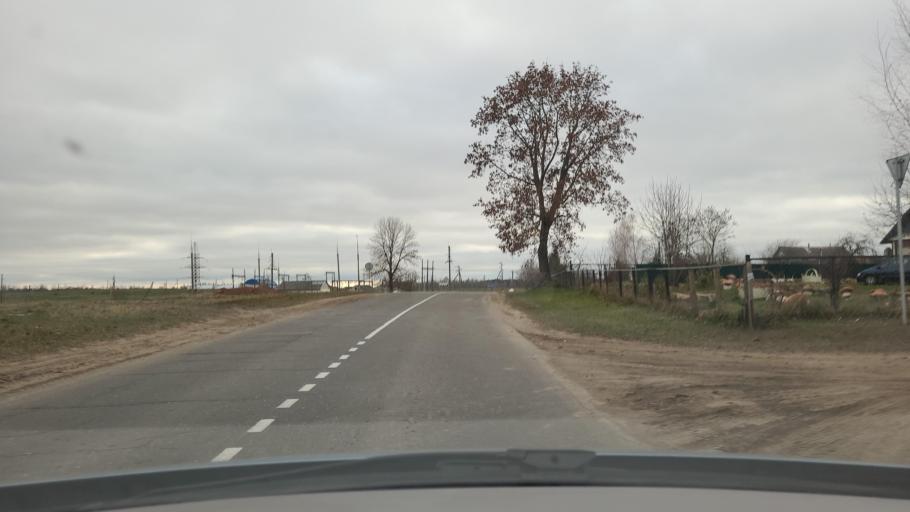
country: BY
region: Minsk
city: Khalopyenichy
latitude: 54.5090
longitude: 28.9600
